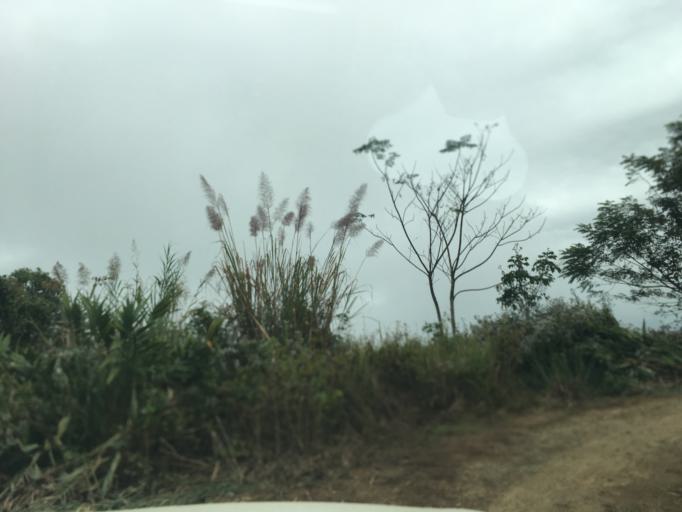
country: LA
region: Houaphan
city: Viengthong
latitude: 19.9395
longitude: 103.2992
